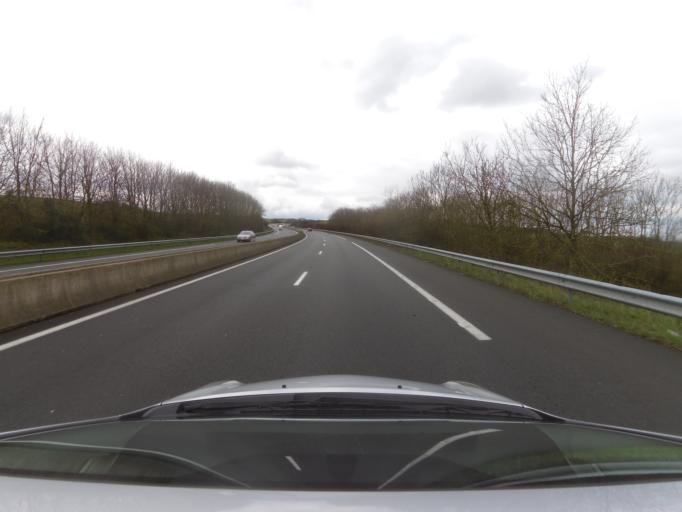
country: FR
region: Nord-Pas-de-Calais
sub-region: Departement du Pas-de-Calais
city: Wimille
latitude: 50.7814
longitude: 1.6562
